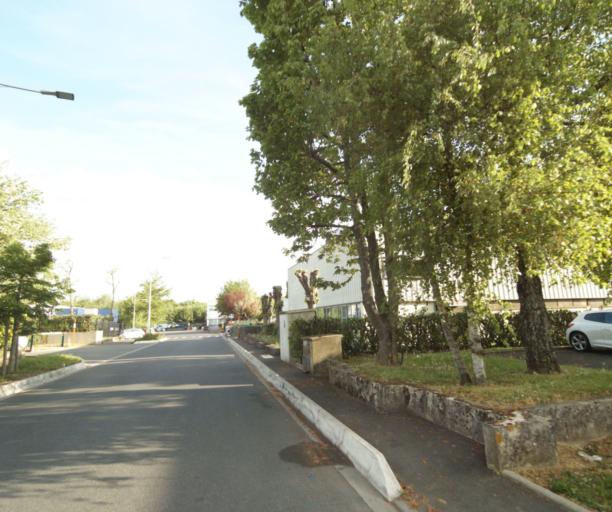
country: FR
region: Ile-de-France
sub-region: Departement de Seine-et-Marne
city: Torcy
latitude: 48.8449
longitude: 2.6561
